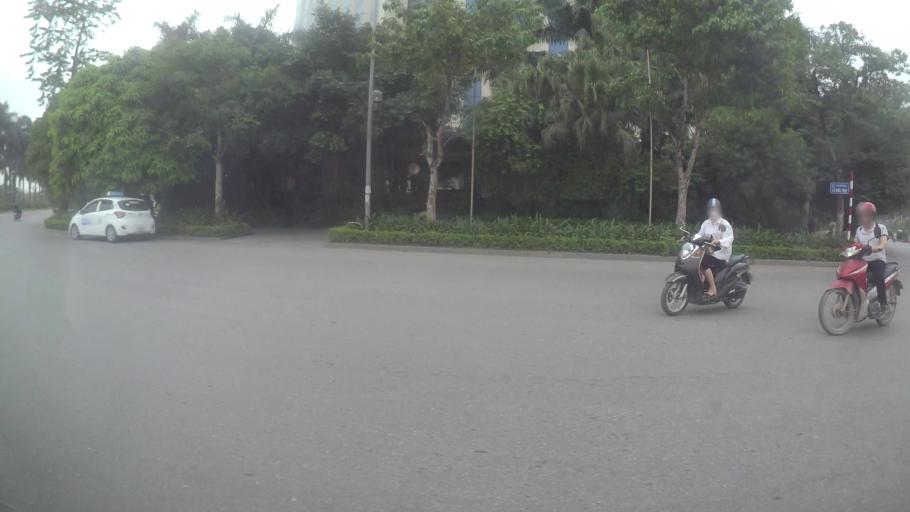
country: VN
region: Ha Noi
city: Cau Dien
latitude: 21.0277
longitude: 105.7680
